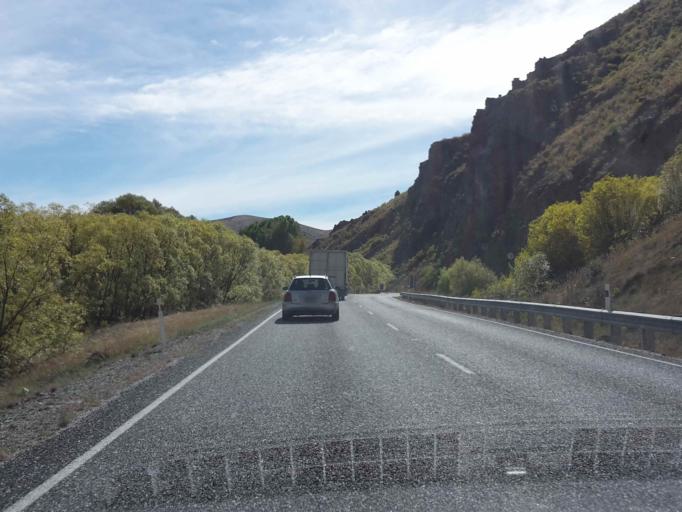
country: NZ
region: Otago
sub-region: Queenstown-Lakes District
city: Wanaka
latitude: -44.7218
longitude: 169.5065
